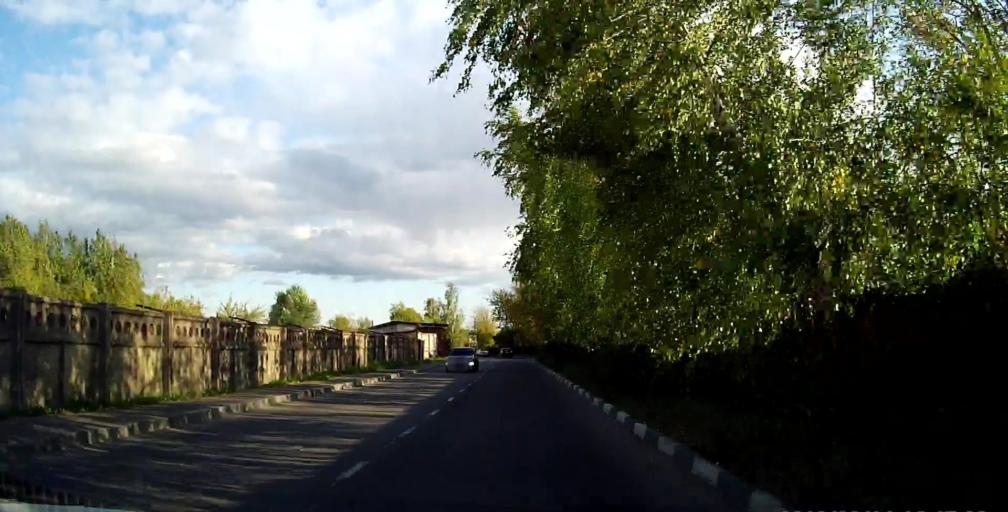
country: RU
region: Moskovskaya
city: Klimovsk
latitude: 55.3670
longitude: 37.5474
